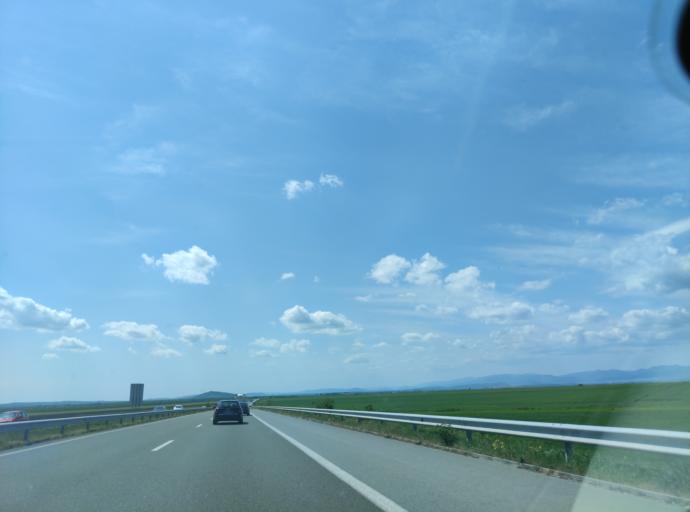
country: BG
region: Yambol
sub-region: Obshtina Yambol
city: Yambol
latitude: 42.5557
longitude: 26.5736
